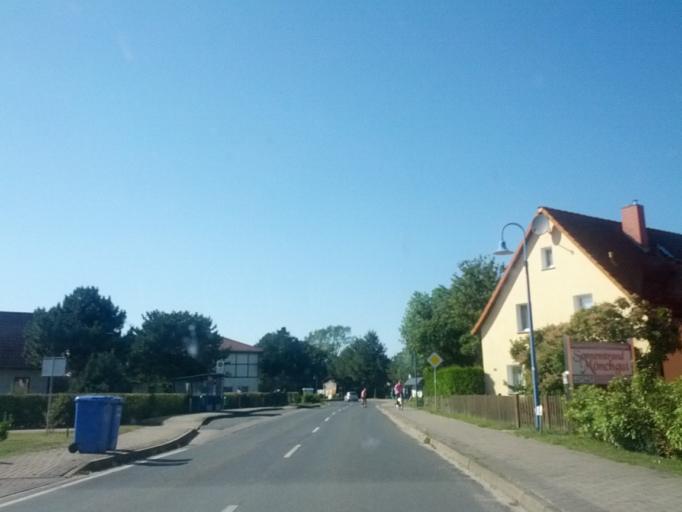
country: DE
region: Mecklenburg-Vorpommern
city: Ostseebad Gohren
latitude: 54.3179
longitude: 13.7196
